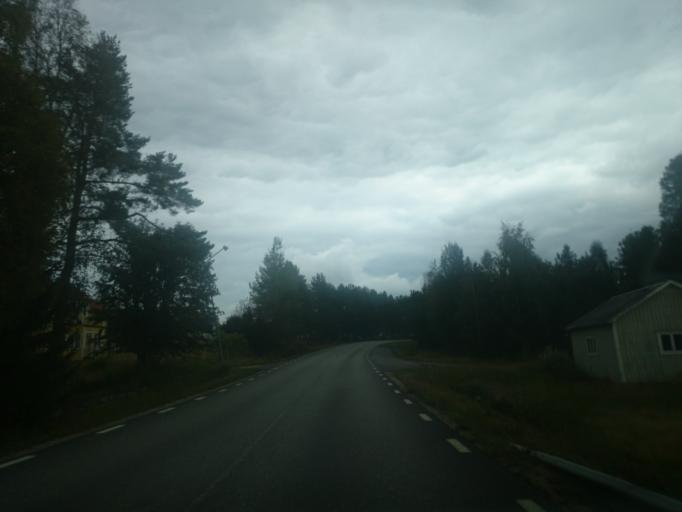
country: SE
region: Jaemtland
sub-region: Harjedalens Kommun
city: Sveg
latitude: 61.9958
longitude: 15.0077
